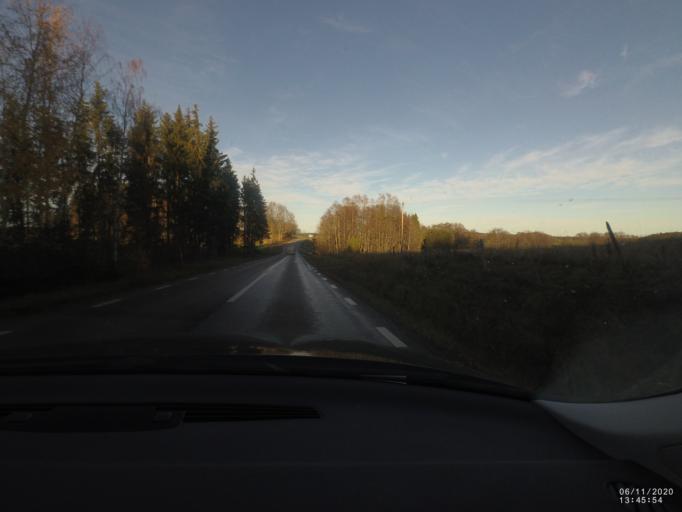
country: SE
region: Soedermanland
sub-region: Nykopings Kommun
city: Nykoping
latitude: 58.8816
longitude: 17.0883
